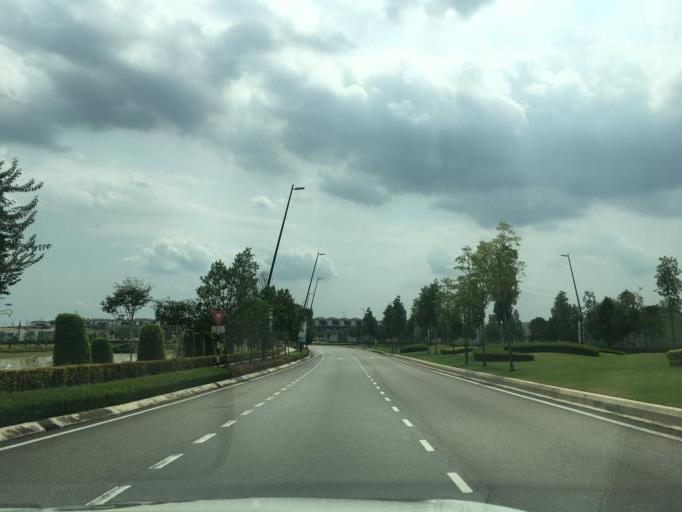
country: MY
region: Selangor
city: Shah Alam
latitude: 3.0969
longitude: 101.4801
